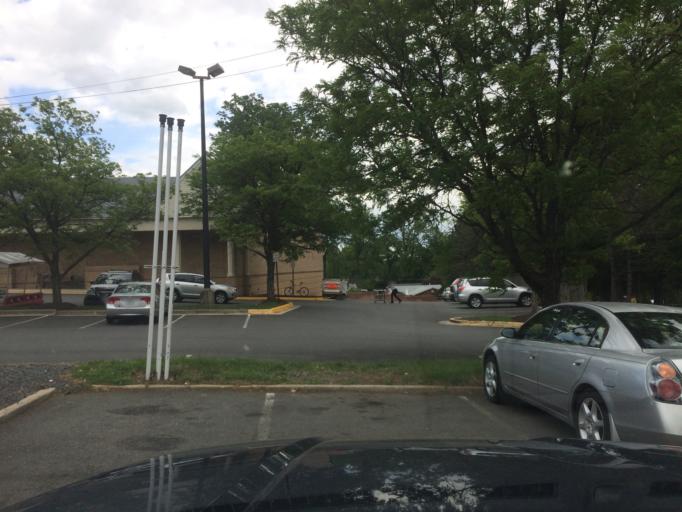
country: US
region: Virginia
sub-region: Fairfax County
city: Jefferson
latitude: 38.8755
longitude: -77.1993
